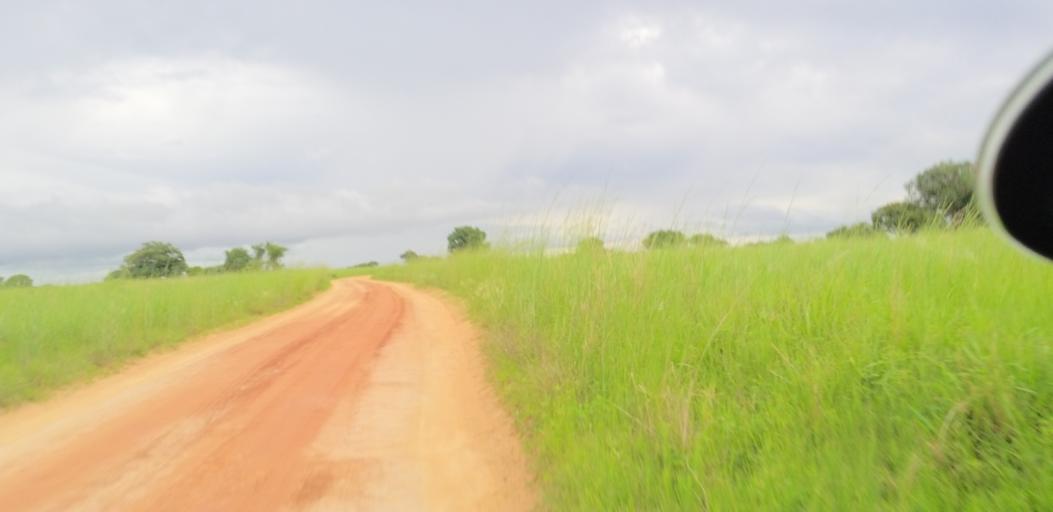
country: ZM
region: Lusaka
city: Chongwe
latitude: -15.1703
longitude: 28.4699
